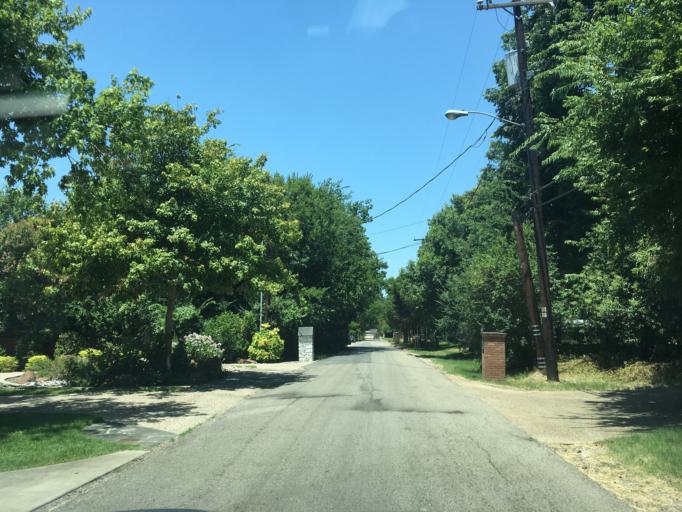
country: US
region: Texas
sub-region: Dallas County
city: Highland Park
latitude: 32.8360
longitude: -96.7293
